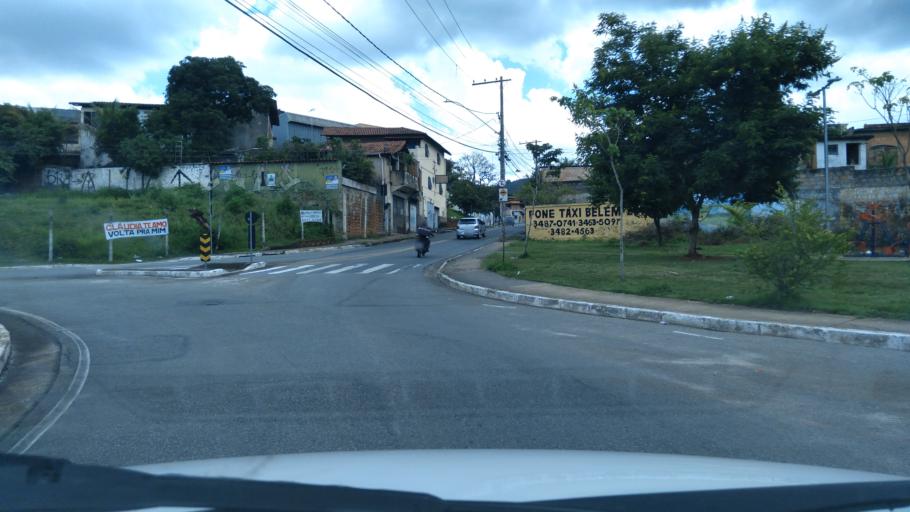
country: BR
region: Minas Gerais
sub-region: Belo Horizonte
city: Belo Horizonte
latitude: -19.9179
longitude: -43.9023
